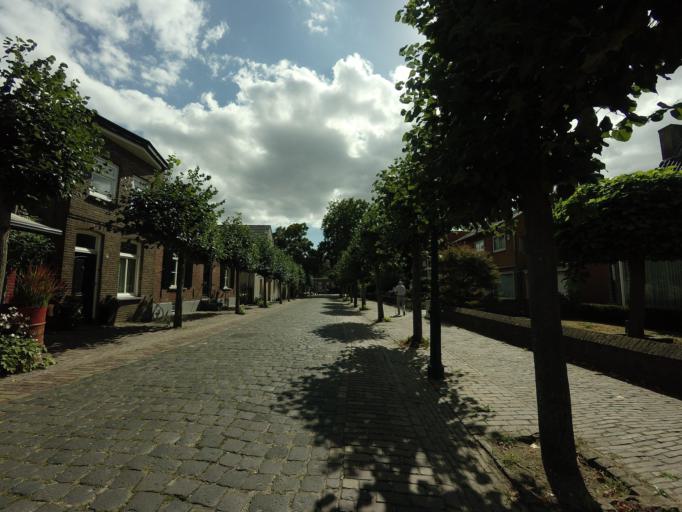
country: NL
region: North Brabant
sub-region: Gemeente Landerd
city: Schaijk
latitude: 51.7957
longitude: 5.6506
